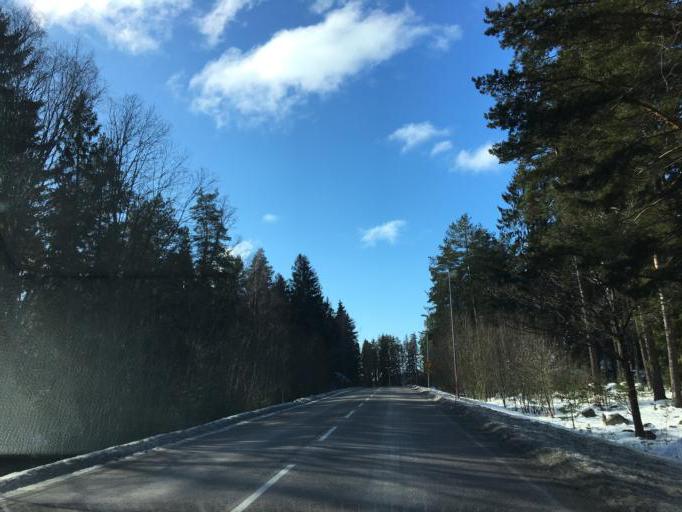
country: SE
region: Vaestmanland
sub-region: Vasteras
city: Vasteras
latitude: 59.6048
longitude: 16.4590
